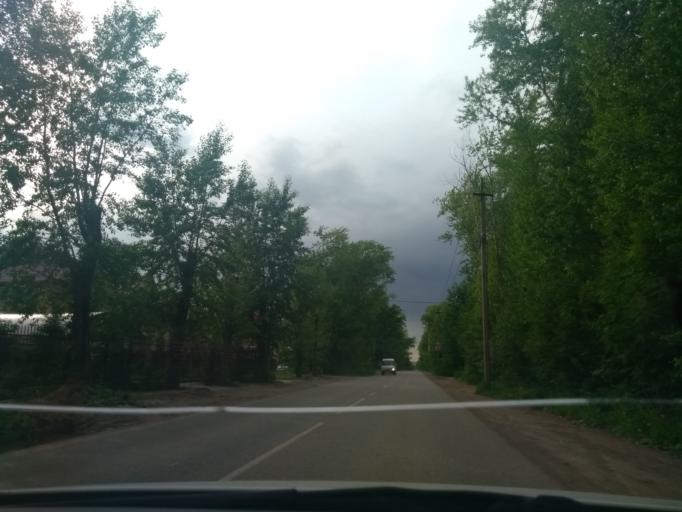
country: RU
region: Perm
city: Perm
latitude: 57.9978
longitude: 56.3354
